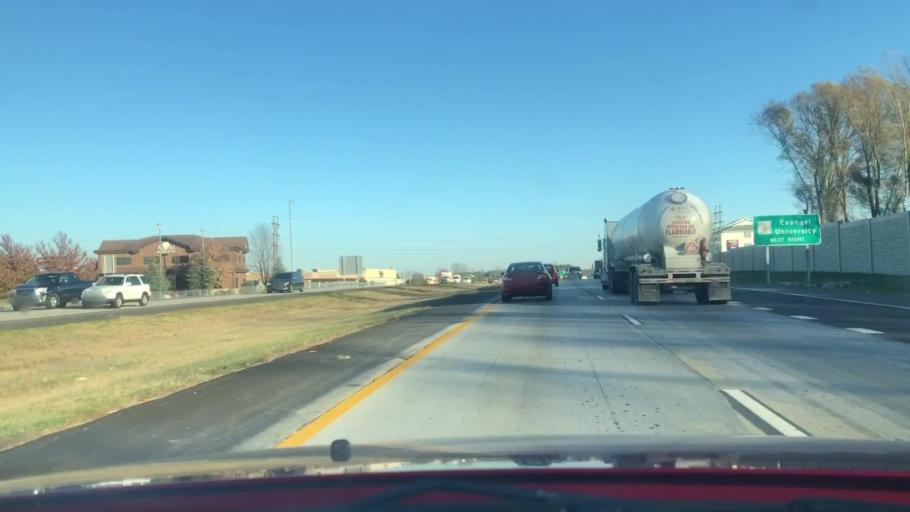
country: US
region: Missouri
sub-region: Greene County
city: Springfield
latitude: 37.1415
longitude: -93.2649
